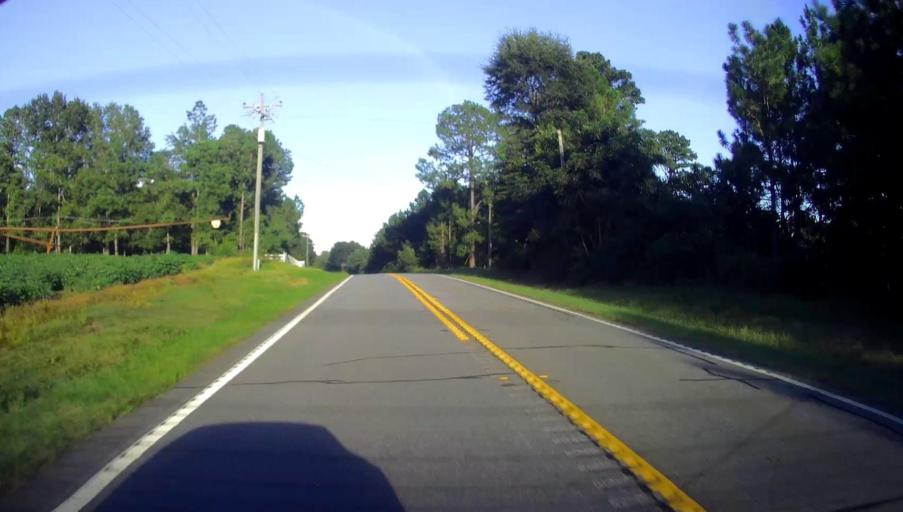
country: US
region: Georgia
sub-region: Pulaski County
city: Hawkinsville
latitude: 32.2658
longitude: -83.5283
